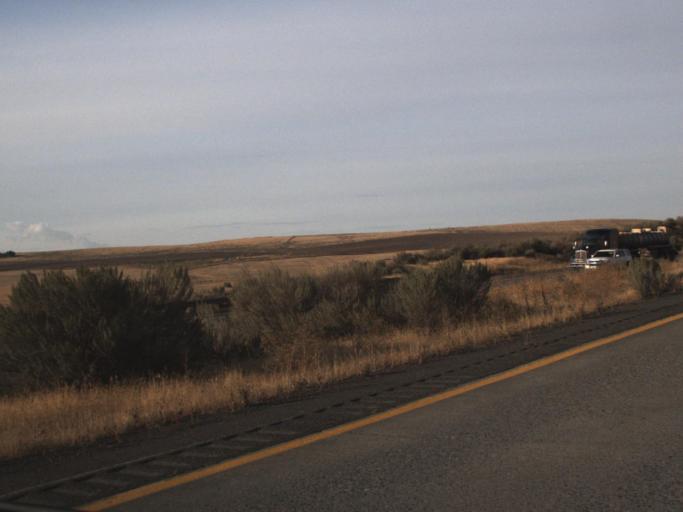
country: US
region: Oregon
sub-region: Umatilla County
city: Umatilla
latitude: 45.9738
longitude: -119.3360
